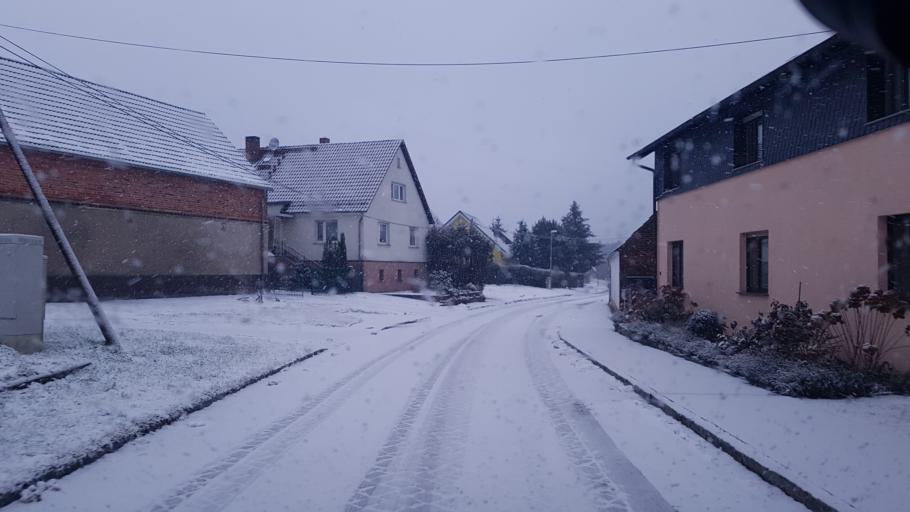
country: DE
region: Brandenburg
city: Schenkendobern
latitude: 51.9099
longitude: 14.5757
